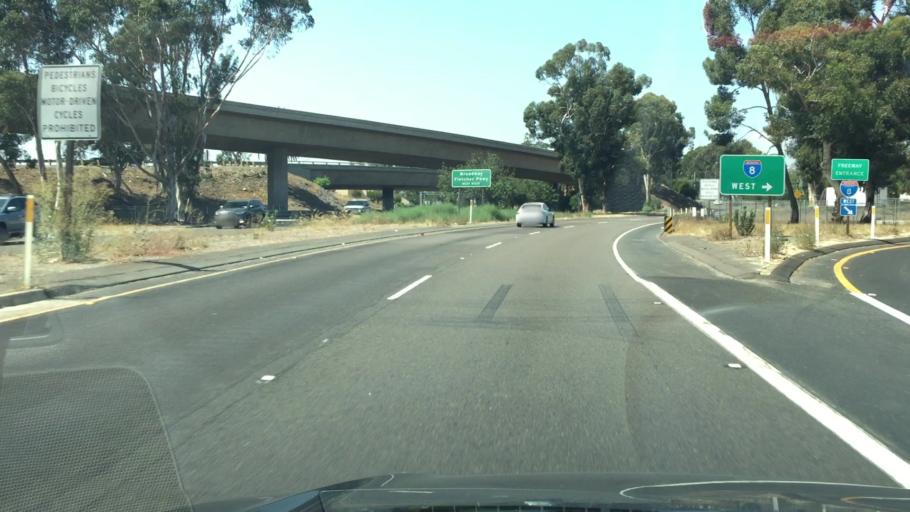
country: US
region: California
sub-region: San Diego County
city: El Cajon
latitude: 32.8036
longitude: -116.9623
